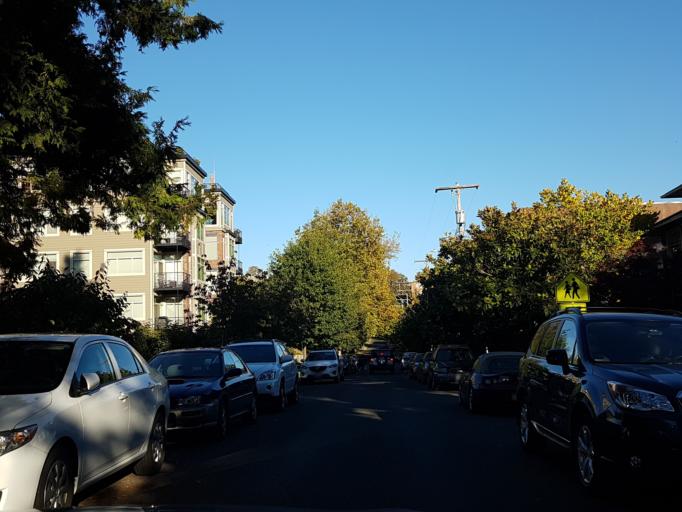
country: US
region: Washington
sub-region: King County
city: Seattle
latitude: 47.6305
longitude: -122.3603
